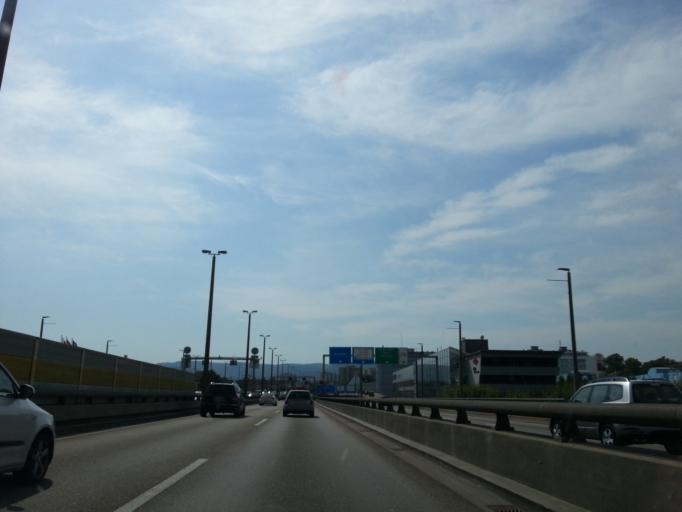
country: CH
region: Basel-Landschaft
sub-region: Bezirk Arlesheim
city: Birsfelden
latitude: 47.5579
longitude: 7.6139
